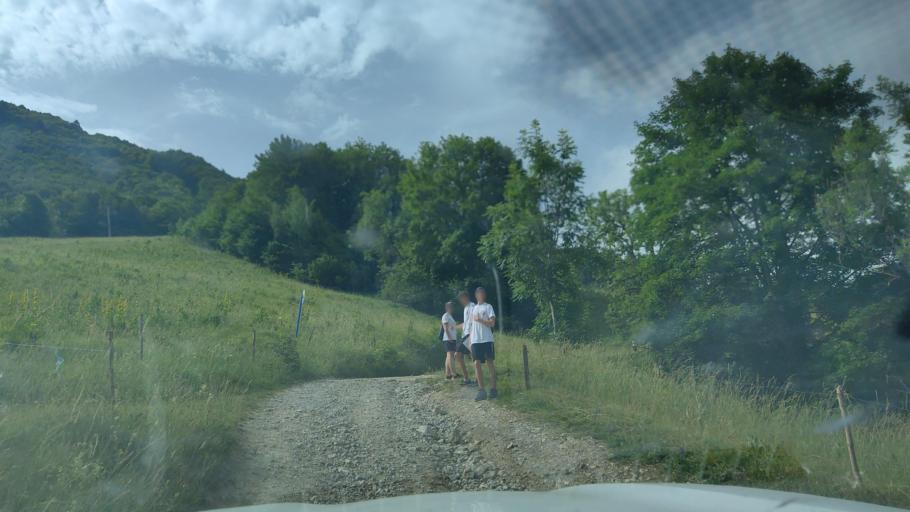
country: FR
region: Rhone-Alpes
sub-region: Departement de la Savoie
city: Cruet
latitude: 45.6047
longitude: 6.1098
